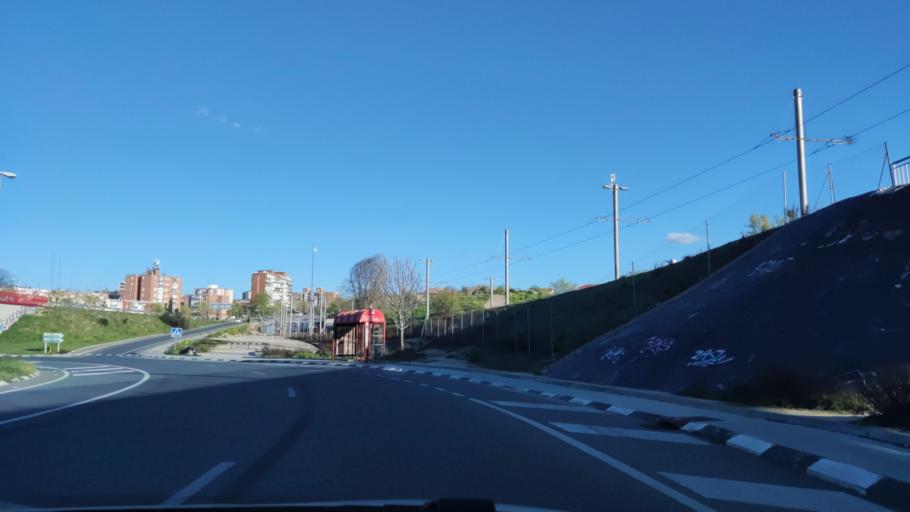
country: ES
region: Madrid
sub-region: Provincia de Madrid
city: Latina
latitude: 40.3995
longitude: -3.7794
